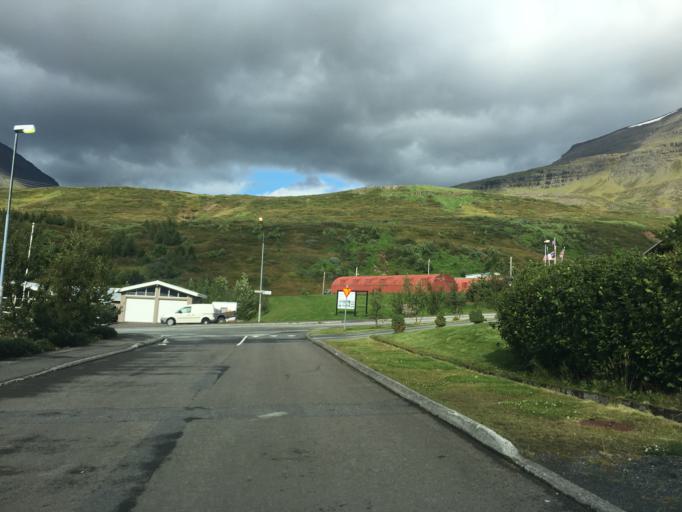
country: IS
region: East
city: Reydarfjoerdur
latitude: 65.0370
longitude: -14.2098
